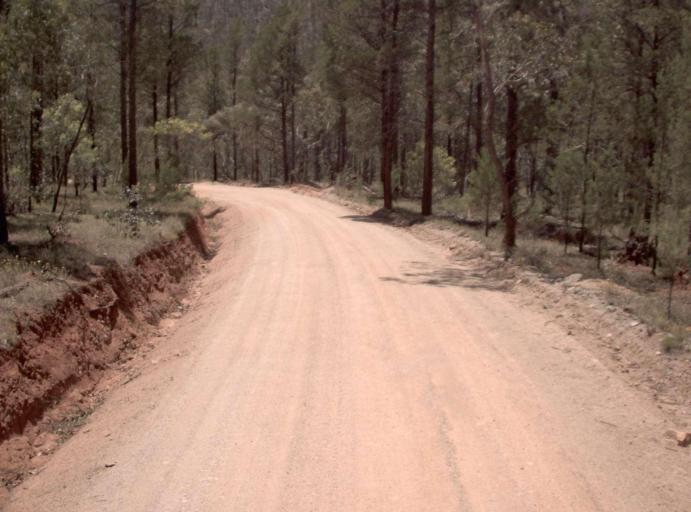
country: AU
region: New South Wales
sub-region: Snowy River
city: Jindabyne
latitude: -36.8955
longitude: 148.4220
